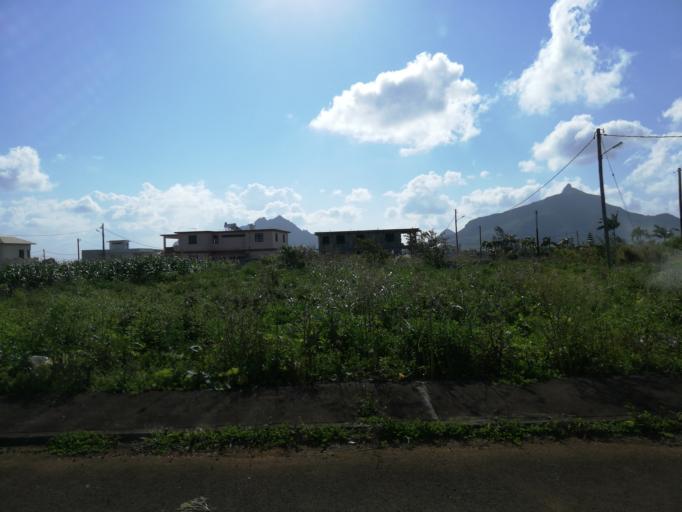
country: MU
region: Moka
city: Verdun
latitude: -20.2250
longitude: 57.5475
